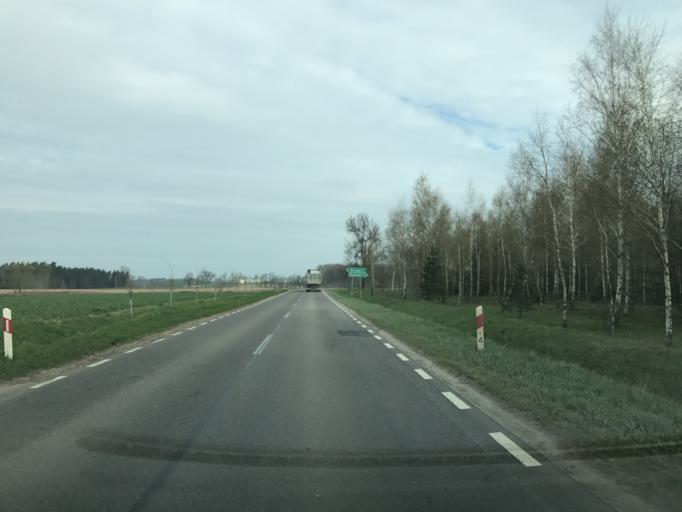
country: PL
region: Warmian-Masurian Voivodeship
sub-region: Powiat ostrodzki
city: Gierzwald
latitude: 53.5265
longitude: 20.0893
